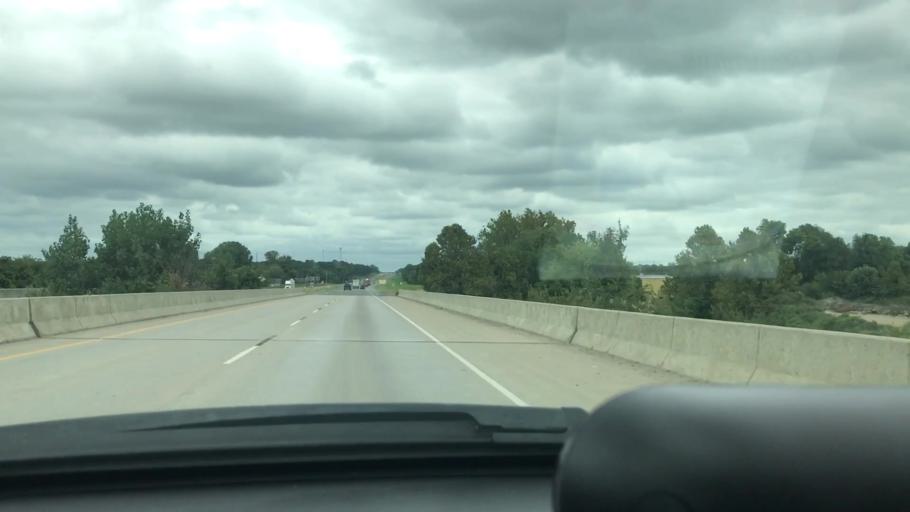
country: US
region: Oklahoma
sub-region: Muskogee County
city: Muskogee
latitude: 35.8104
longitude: -95.4022
